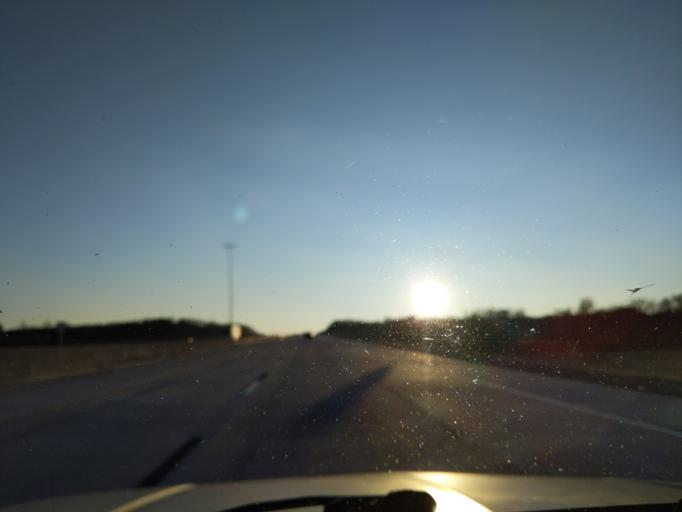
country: US
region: Oklahoma
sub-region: Creek County
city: Kellyville
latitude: 35.9094
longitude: -96.3015
